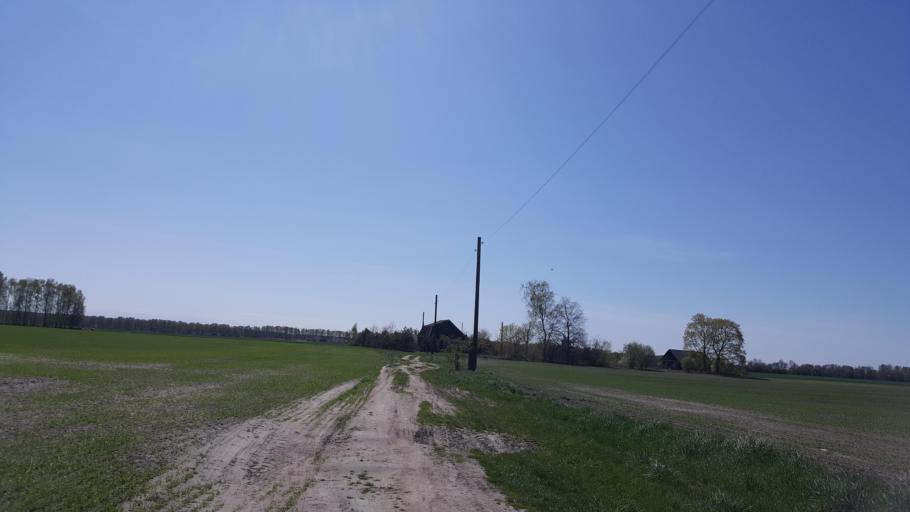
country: BY
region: Brest
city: Kamyanyets
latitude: 52.3262
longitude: 23.7613
